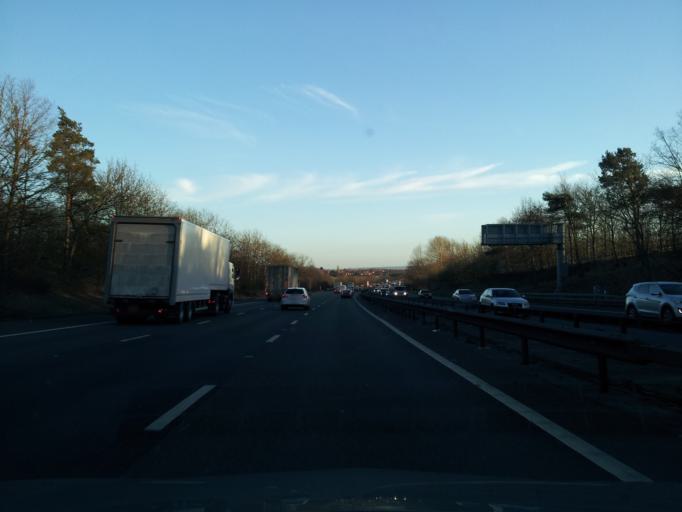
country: GB
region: England
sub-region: Milton Keynes
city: Gayhurst
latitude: 52.0976
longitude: -0.7630
